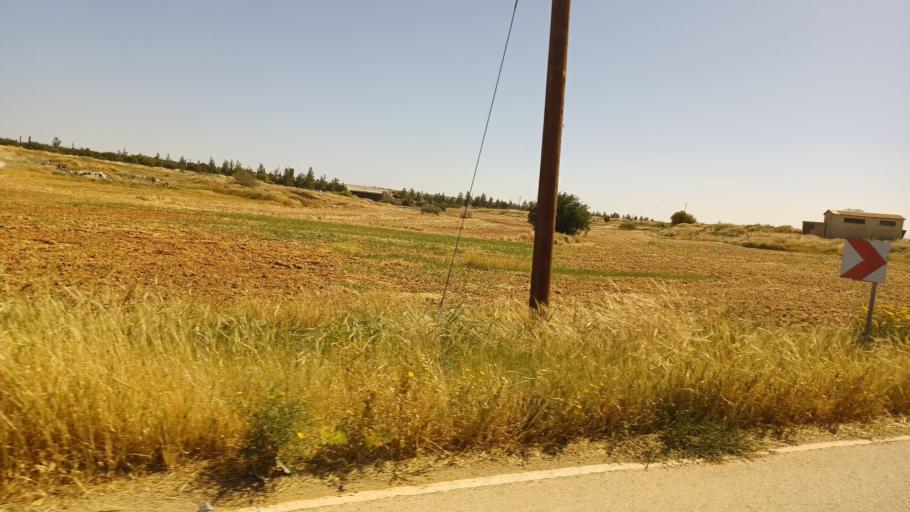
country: CY
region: Lefkosia
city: Kokkinotrimithia
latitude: 35.1587
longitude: 33.1719
